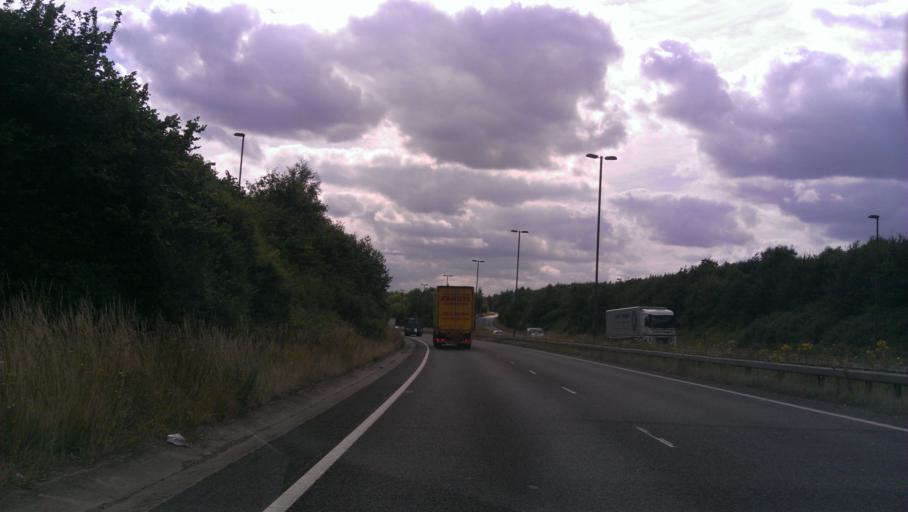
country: GB
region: England
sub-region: Kent
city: Strood
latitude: 51.4108
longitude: 0.4725
